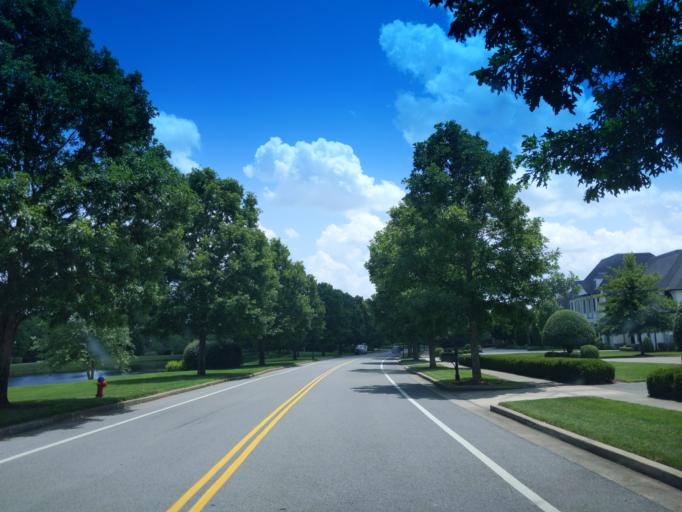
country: US
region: Tennessee
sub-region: Williamson County
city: Brentwood Estates
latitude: 36.0236
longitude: -86.7701
